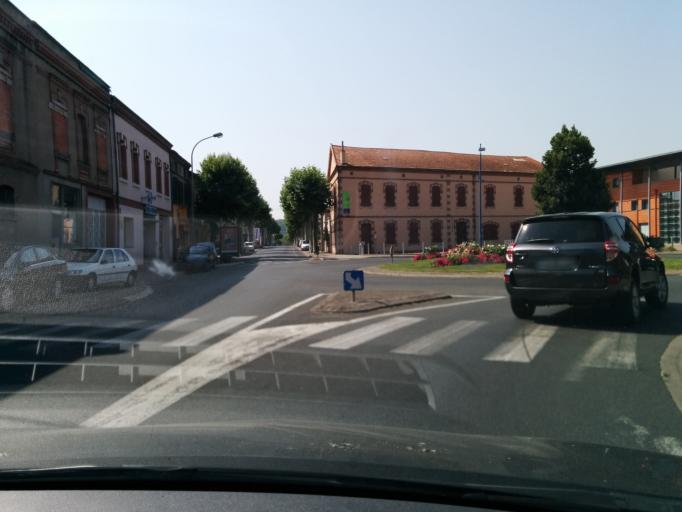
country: FR
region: Midi-Pyrenees
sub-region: Departement du Tarn
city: Albi
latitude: 43.9407
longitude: 2.1395
